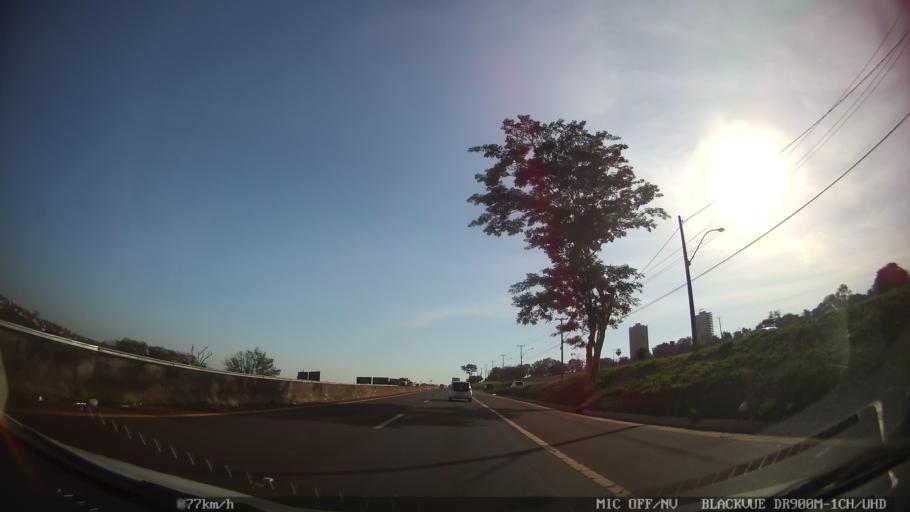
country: BR
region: Sao Paulo
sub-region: Ribeirao Preto
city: Ribeirao Preto
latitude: -21.2455
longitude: -47.8193
